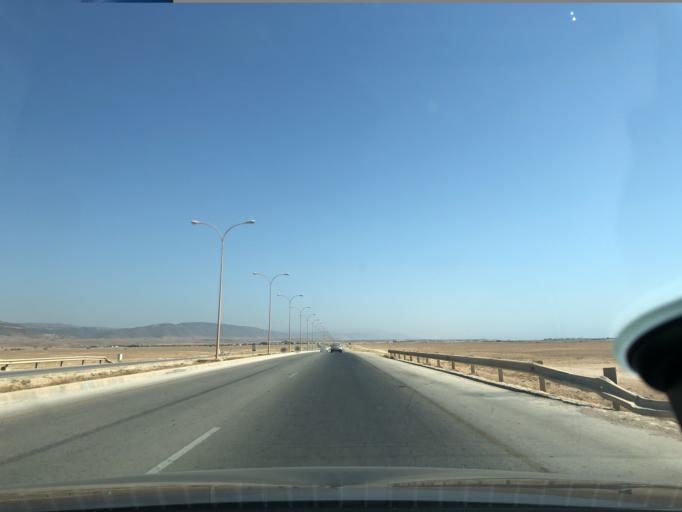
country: OM
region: Zufar
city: Salalah
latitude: 17.0510
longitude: 54.2550
